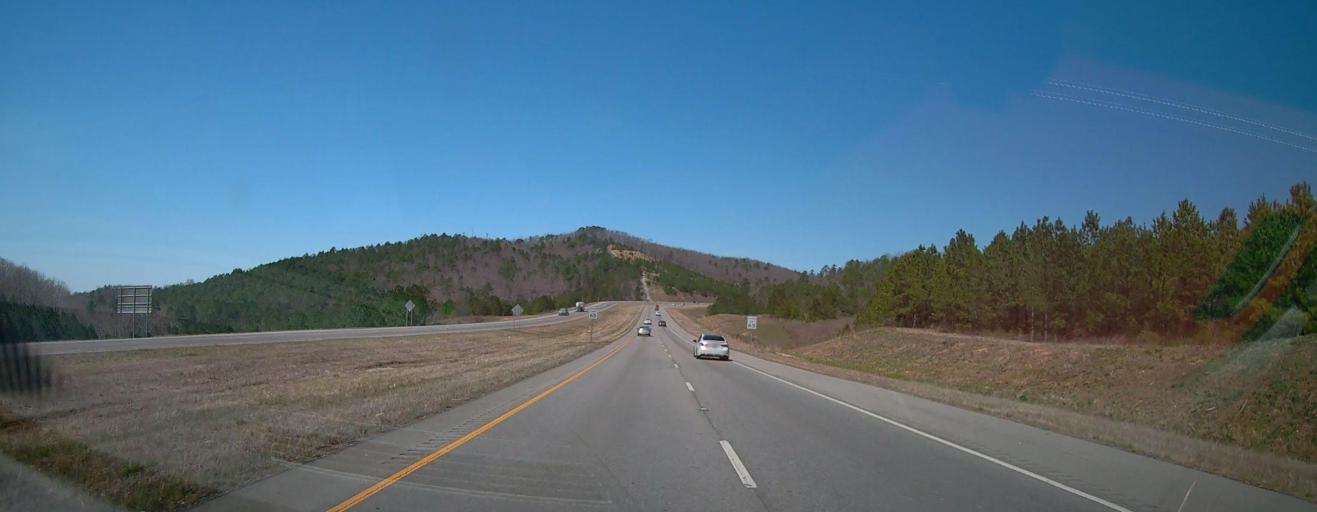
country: US
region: Alabama
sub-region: Calhoun County
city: Anniston
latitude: 33.6761
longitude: -85.7952
